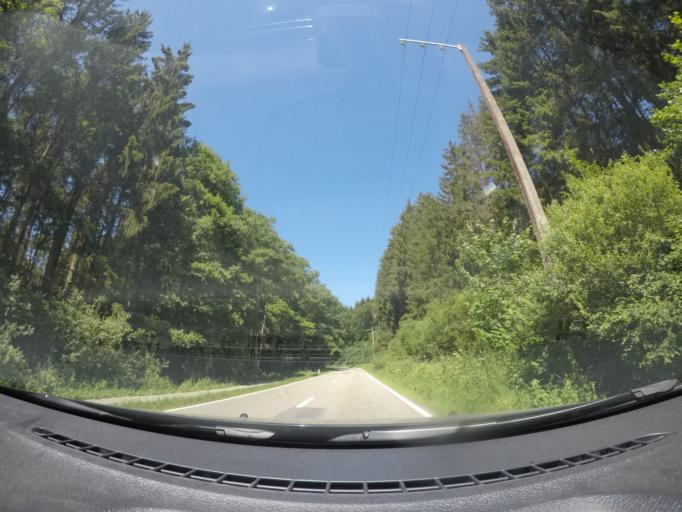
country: BE
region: Wallonia
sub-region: Province du Luxembourg
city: Wellin
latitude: 50.0568
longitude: 5.1416
